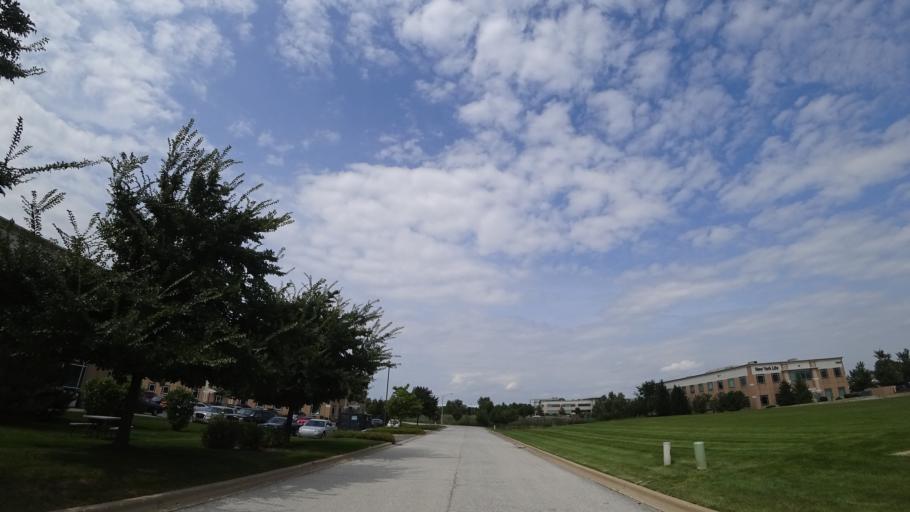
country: US
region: Illinois
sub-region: Cook County
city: Tinley Park
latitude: 41.5513
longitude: -87.8087
